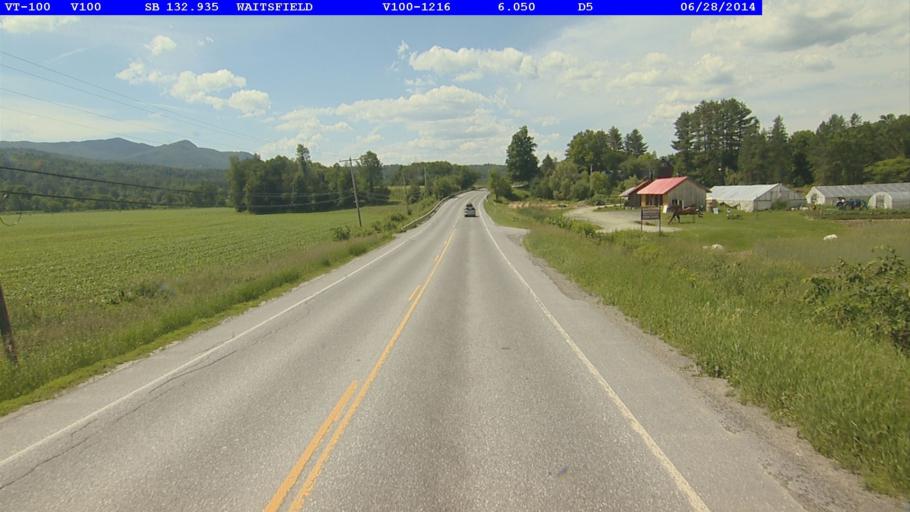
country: US
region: Vermont
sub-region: Washington County
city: Waterbury
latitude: 44.2153
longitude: -72.7925
